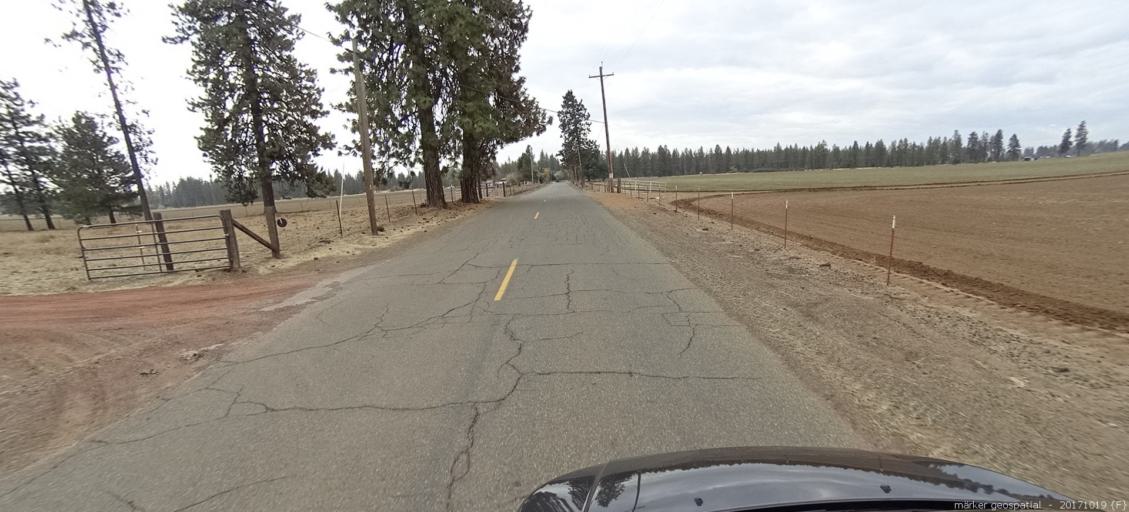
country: US
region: California
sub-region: Shasta County
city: Burney
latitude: 41.0701
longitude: -121.3652
